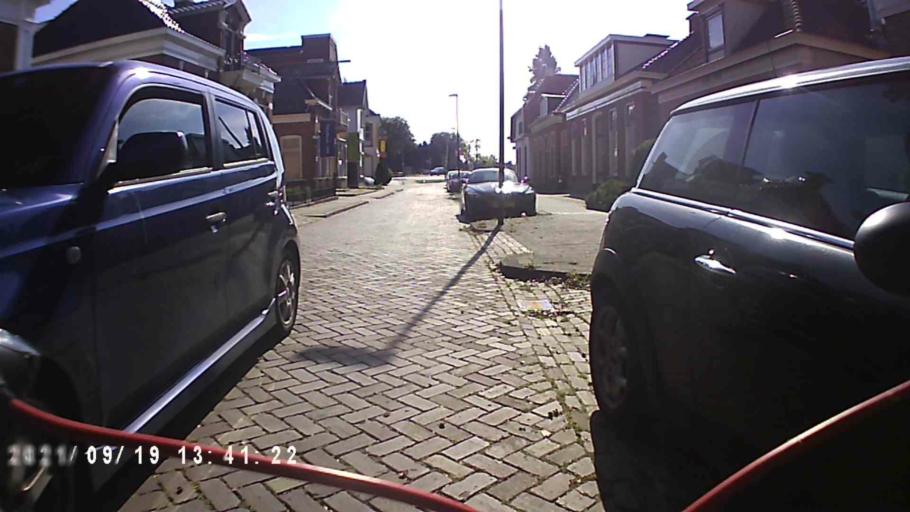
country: NL
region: Groningen
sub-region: Gemeente  Oldambt
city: Winschoten
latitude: 53.1395
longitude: 7.0406
